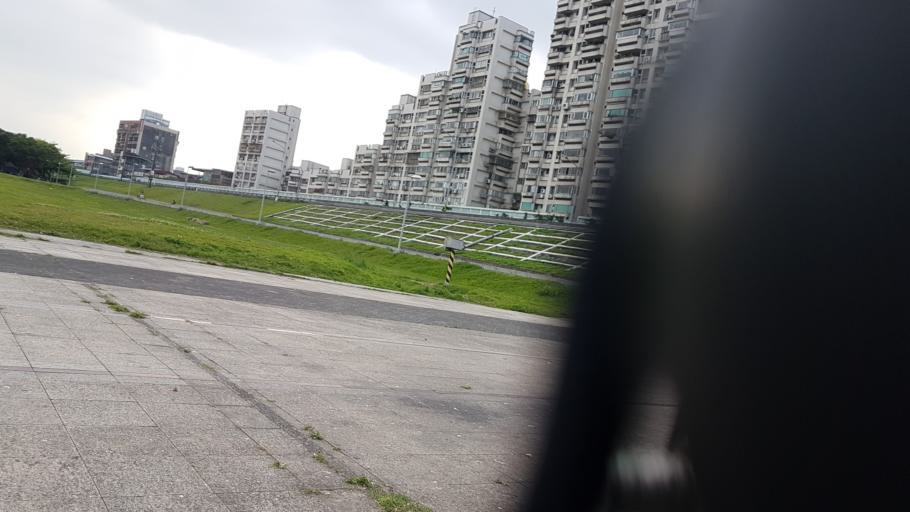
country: TW
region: Taipei
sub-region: Taipei
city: Banqiao
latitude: 25.0192
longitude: 121.5041
